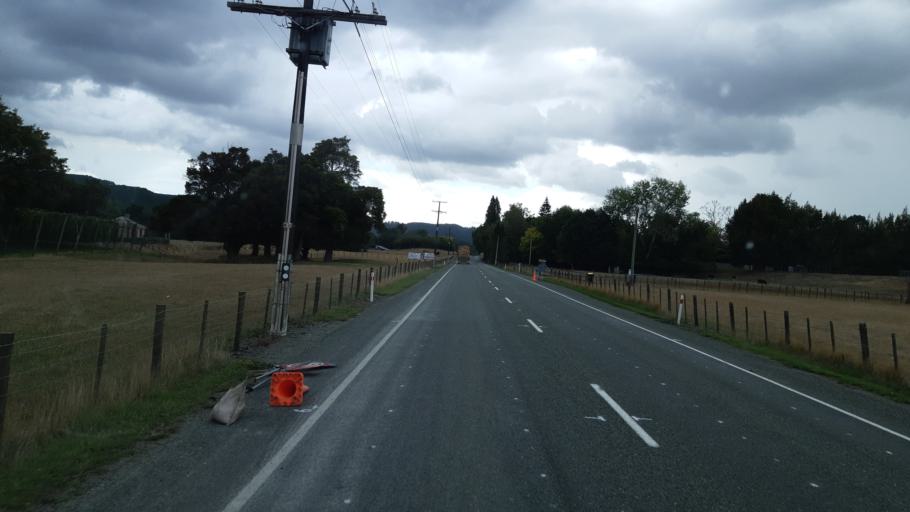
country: NZ
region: Tasman
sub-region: Tasman District
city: Wakefield
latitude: -41.4180
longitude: 173.0091
